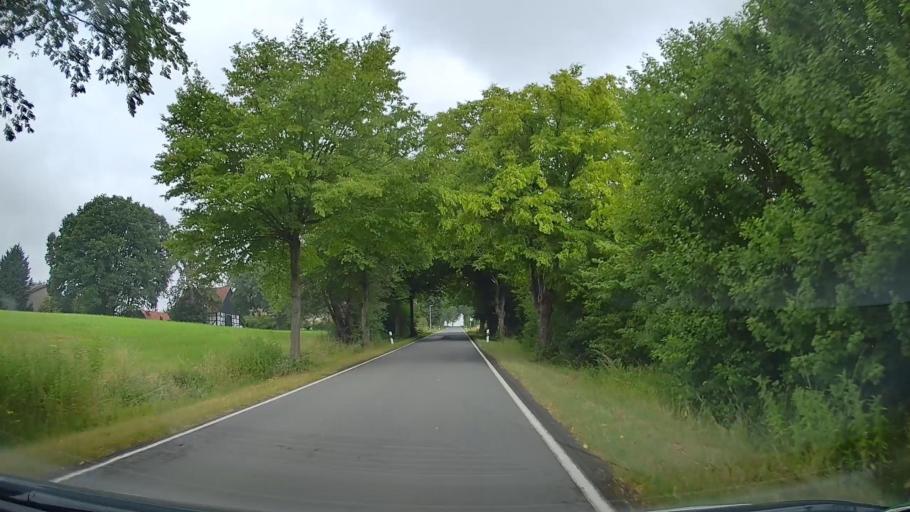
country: DE
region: Lower Saxony
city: Rinteln
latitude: 52.1283
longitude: 9.1021
